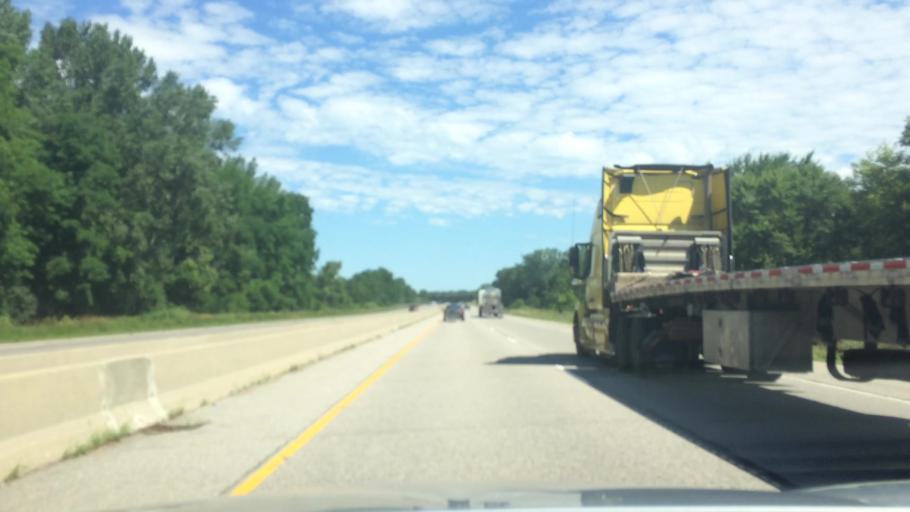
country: US
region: Wisconsin
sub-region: Marquette County
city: Westfield
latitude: 43.7428
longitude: -89.4825
